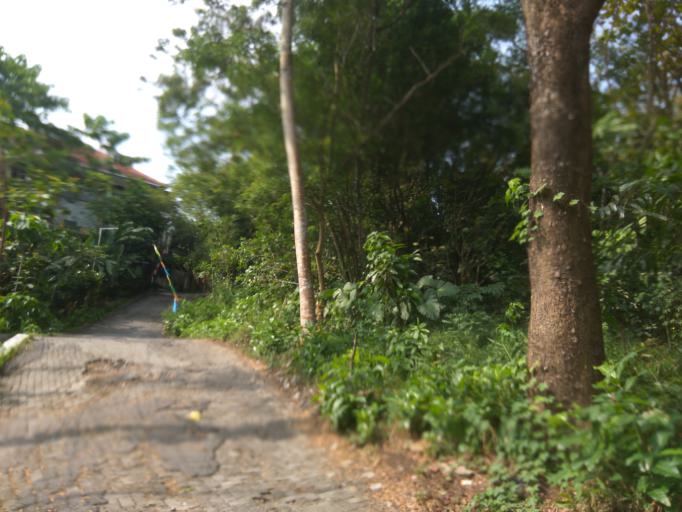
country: ID
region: Central Java
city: Semarang
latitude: -7.0319
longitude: 110.4074
